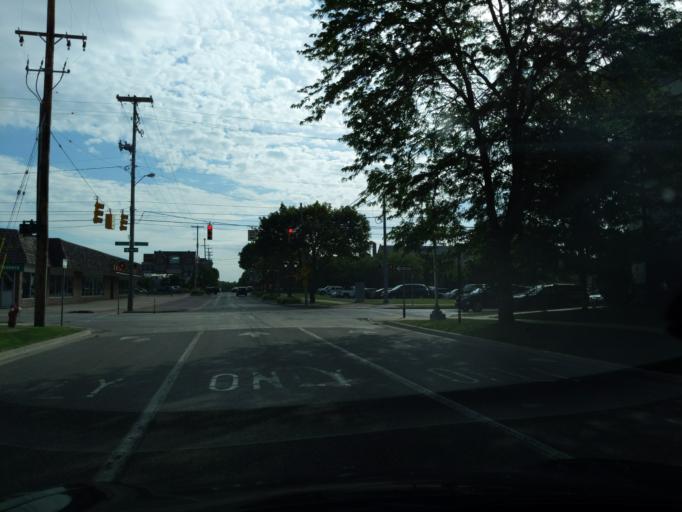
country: US
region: Michigan
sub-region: Midland County
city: Midland
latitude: 43.6152
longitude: -84.2427
